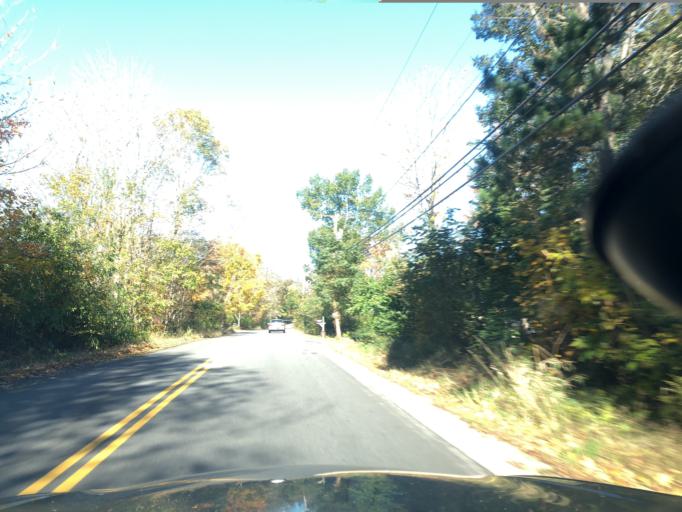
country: US
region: New Hampshire
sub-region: Rockingham County
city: Newmarket
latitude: 43.1088
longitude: -70.9582
